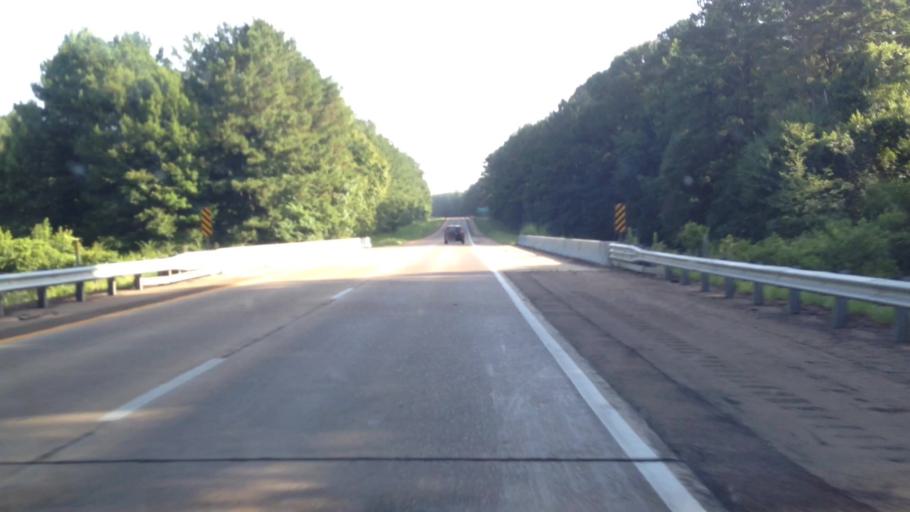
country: US
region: Mississippi
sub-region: Pike County
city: Summit
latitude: 31.3254
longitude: -90.4772
